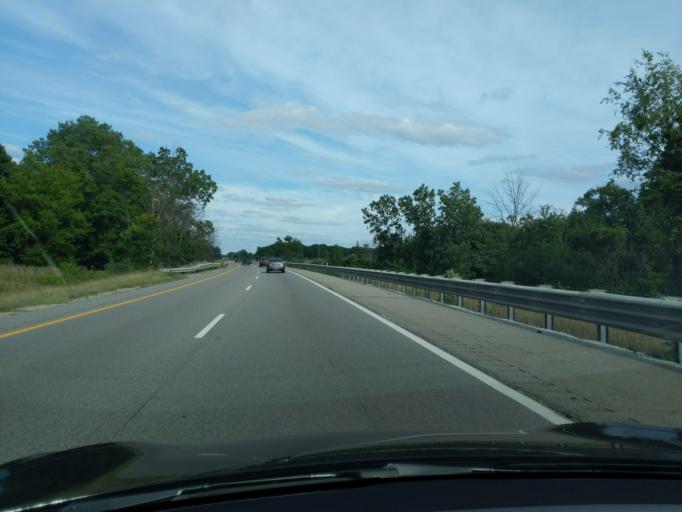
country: US
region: Michigan
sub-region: Ottawa County
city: Coopersville
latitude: 43.0700
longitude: -86.0281
